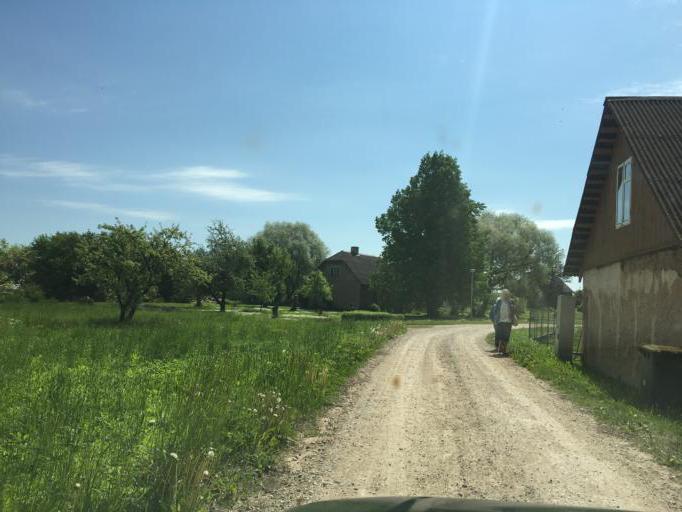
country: LV
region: Talsu Rajons
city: Valdemarpils
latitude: 57.3783
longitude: 22.6020
